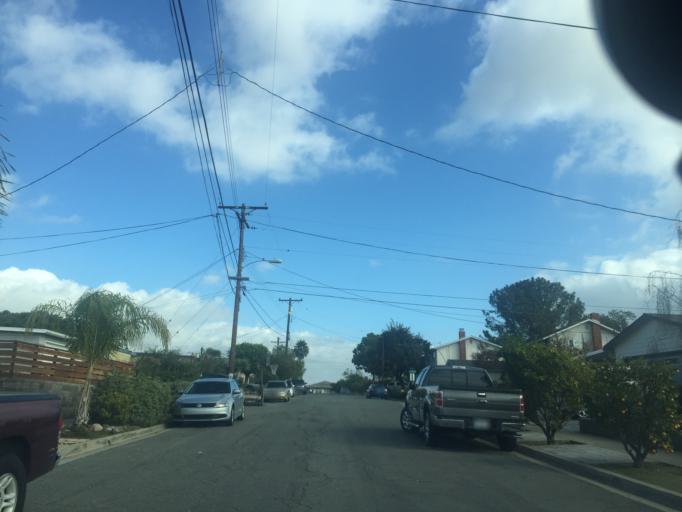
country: US
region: California
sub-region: San Diego County
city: San Diego
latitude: 32.7820
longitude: -117.1520
